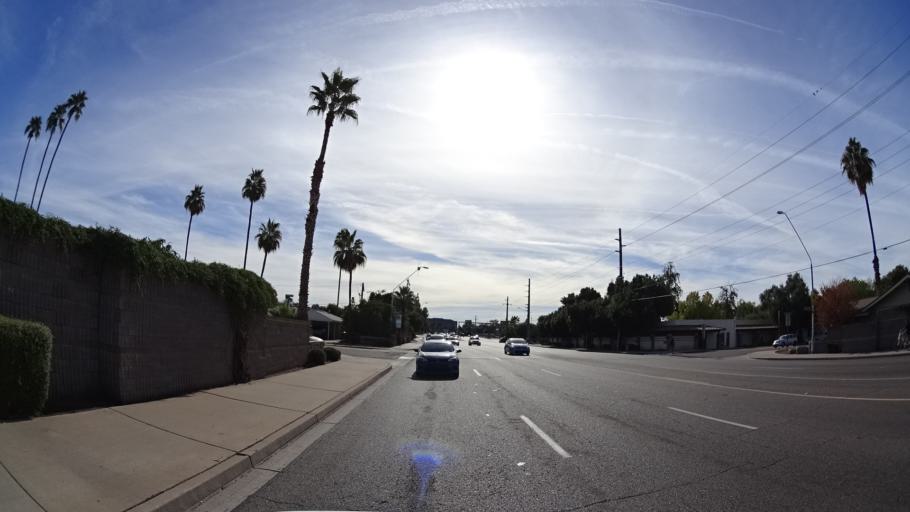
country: US
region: Arizona
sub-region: Maricopa County
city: Tempe Junction
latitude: 33.3880
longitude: -111.9263
